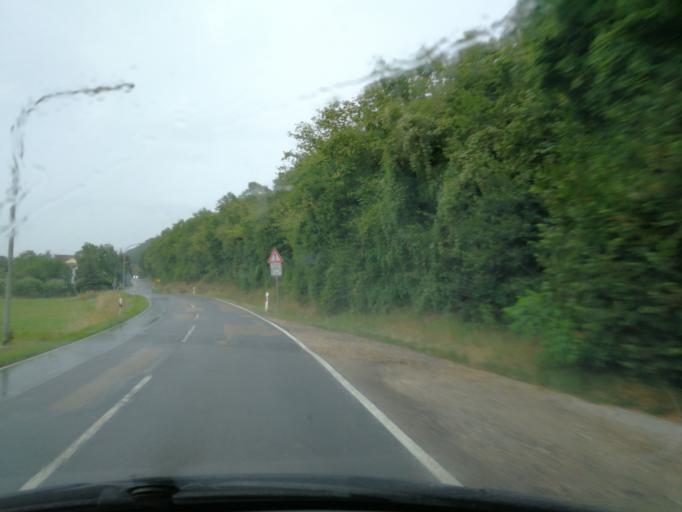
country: DE
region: Bavaria
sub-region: Upper Palatinate
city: Donaustauf
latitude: 49.0230
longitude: 12.2713
